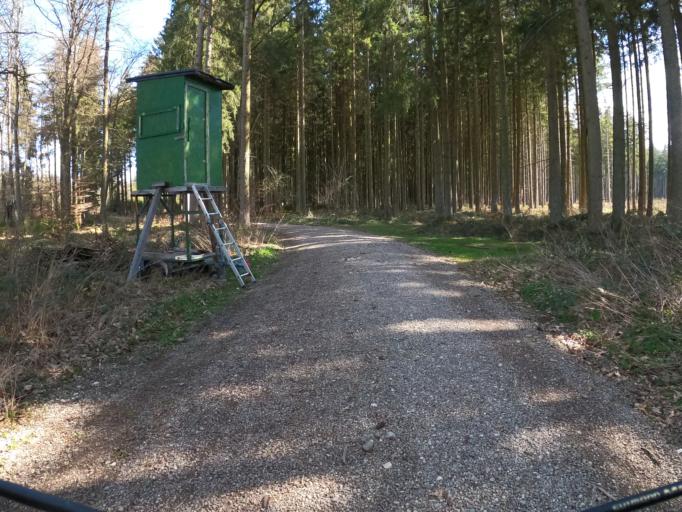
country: DE
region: Bavaria
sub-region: Swabia
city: Nersingen
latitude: 48.4022
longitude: 10.1570
